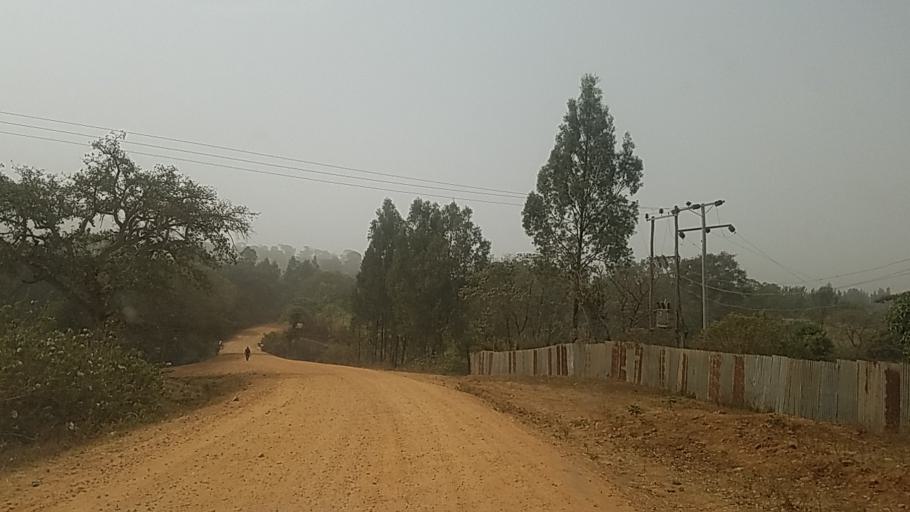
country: ET
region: Amhara
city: Bure
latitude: 10.7796
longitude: 36.2717
